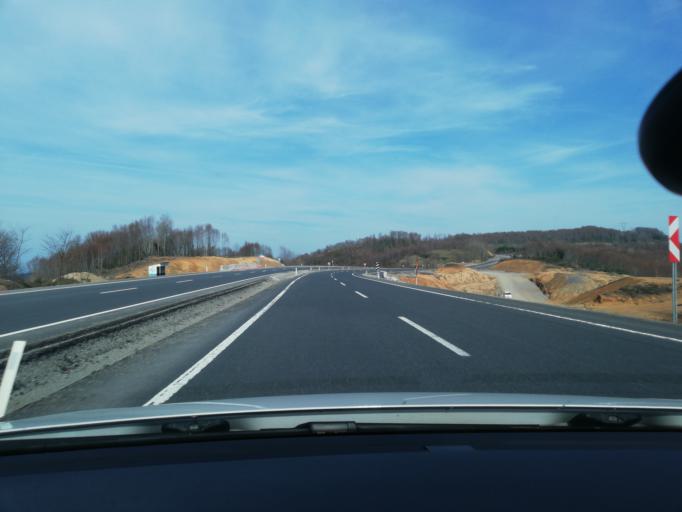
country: TR
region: Zonguldak
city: Ormanli
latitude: 41.3312
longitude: 31.5840
